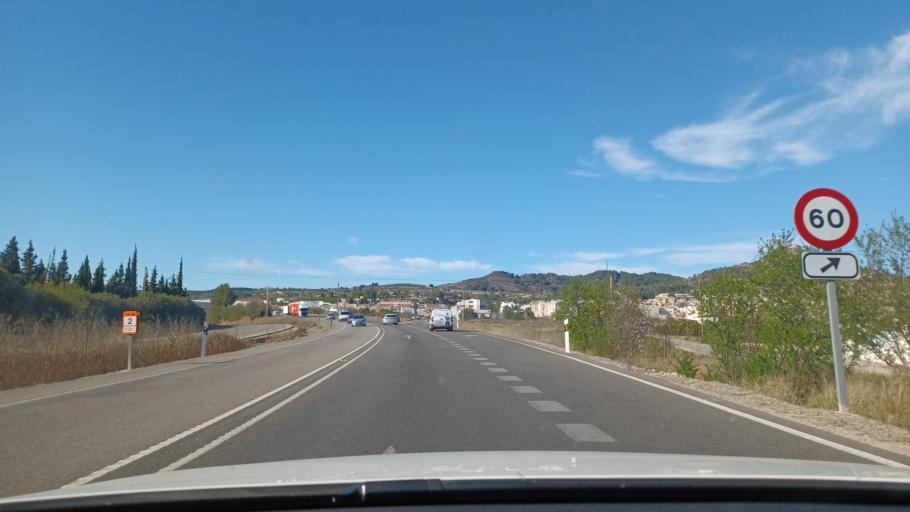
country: ES
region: Valencia
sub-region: Provincia de Valencia
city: Llosa de Ranes
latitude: 39.0111
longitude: -0.5334
